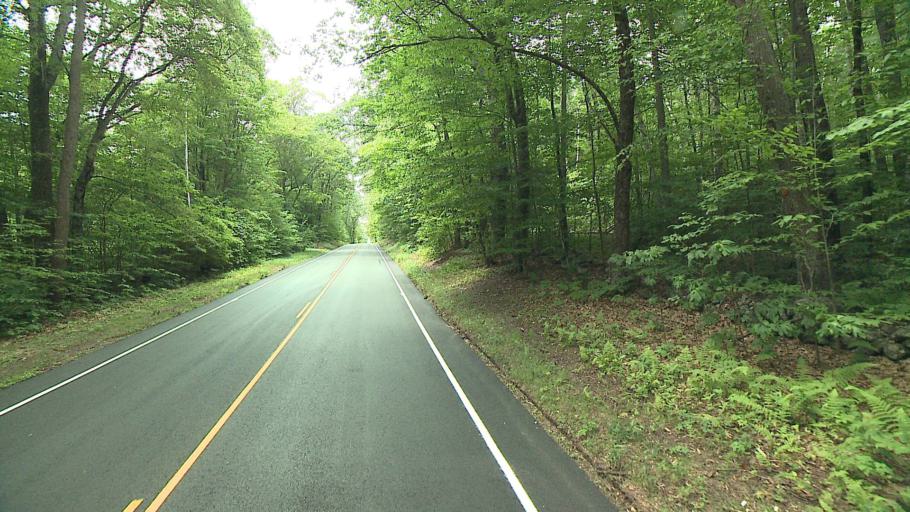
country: US
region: Massachusetts
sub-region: Hampden County
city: Granville
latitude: 42.0165
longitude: -72.8911
